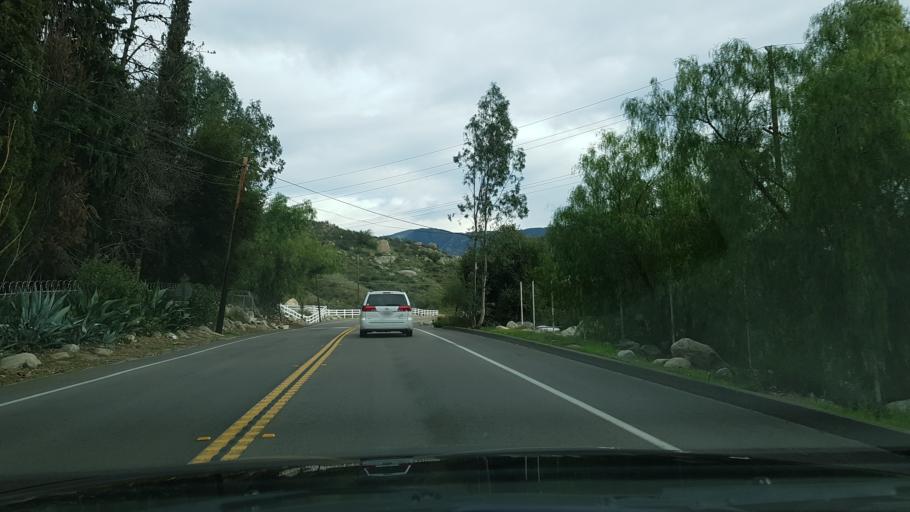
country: US
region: California
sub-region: San Diego County
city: Valley Center
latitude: 33.2856
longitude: -116.9556
